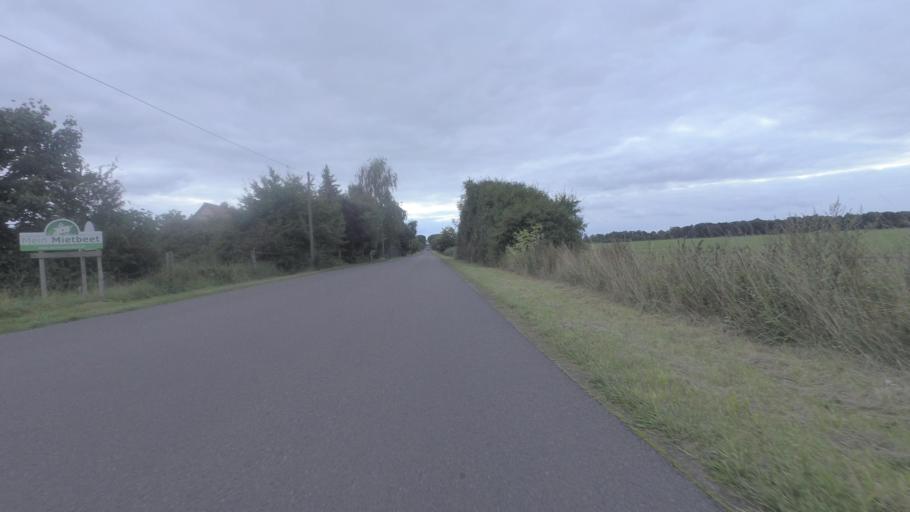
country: DE
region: Brandenburg
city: Neuenhagen
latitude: 52.5670
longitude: 13.6596
